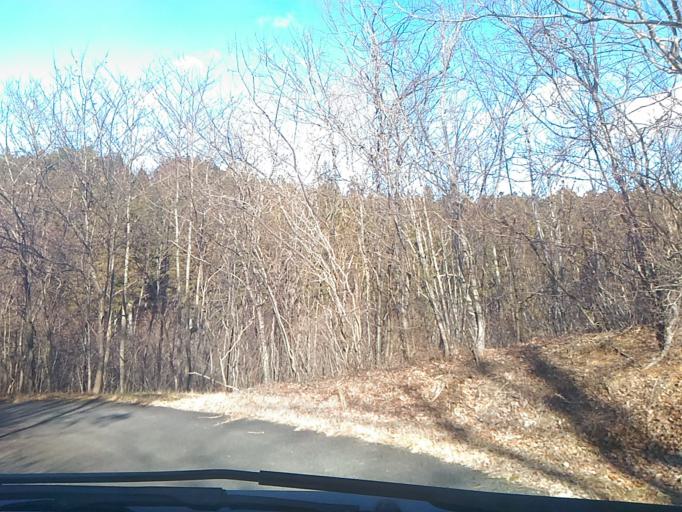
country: JP
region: Fukushima
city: Ishikawa
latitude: 37.0417
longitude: 140.5935
